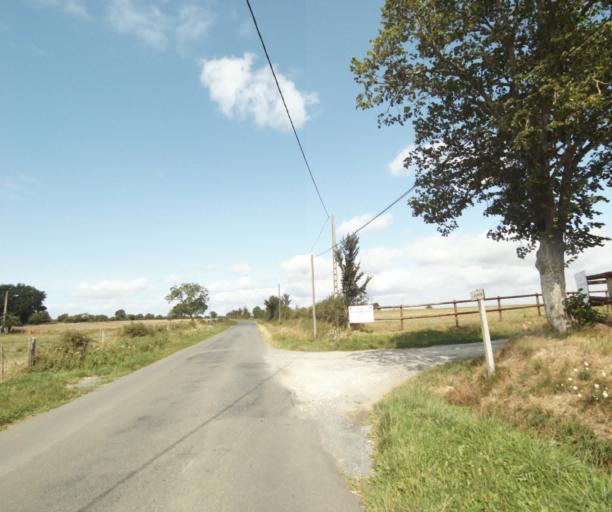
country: FR
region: Pays de la Loire
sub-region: Departement de la Sarthe
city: Sable-sur-Sarthe
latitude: 47.8409
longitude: -0.3646
